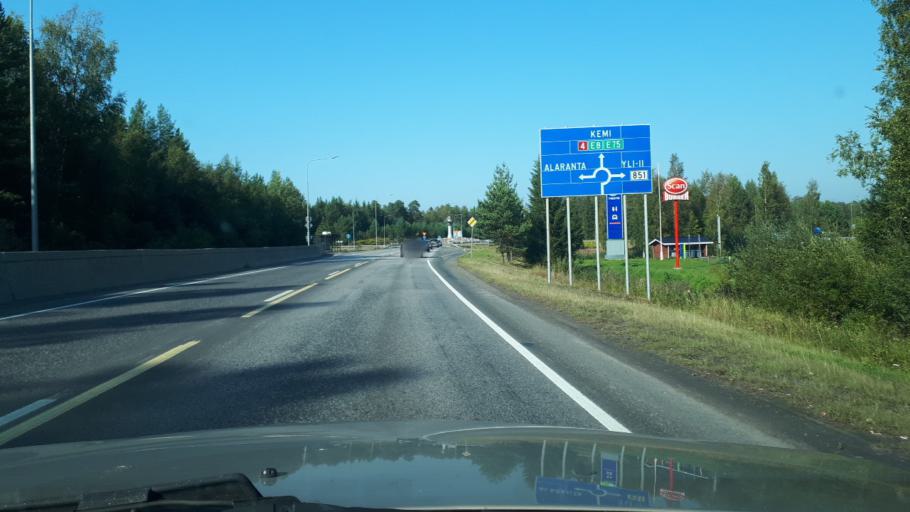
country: FI
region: Northern Ostrobothnia
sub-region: Oulunkaari
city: Ii
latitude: 65.3158
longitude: 25.3732
